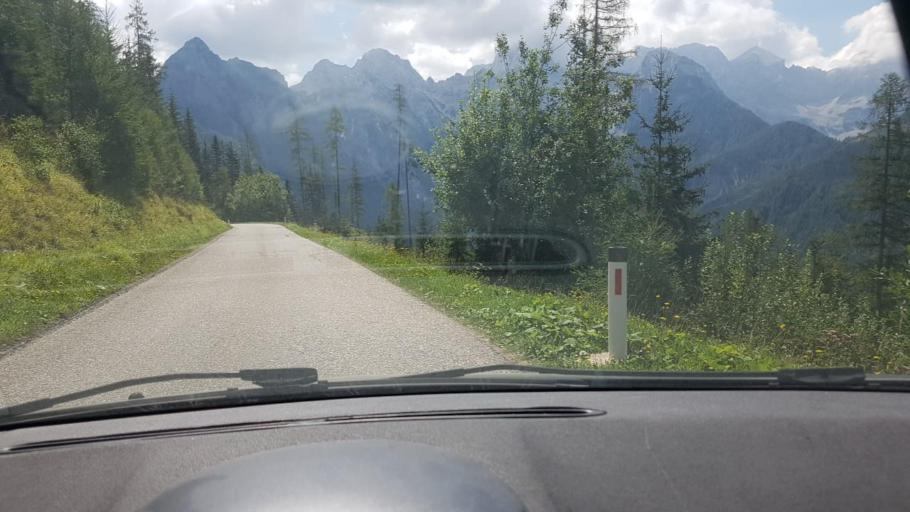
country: SI
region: Jezersko
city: Zgornje Jezersko
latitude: 46.4197
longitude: 14.5724
